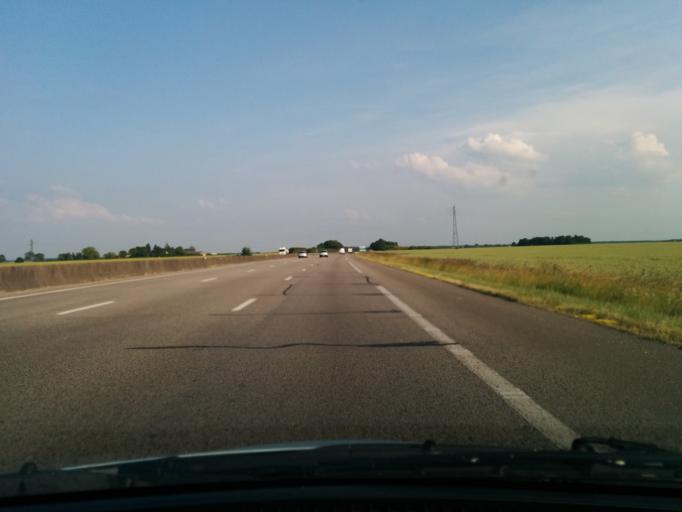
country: FR
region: Haute-Normandie
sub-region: Departement de l'Eure
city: Saint-Aubin-sur-Gaillon
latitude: 49.1292
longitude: 1.3207
